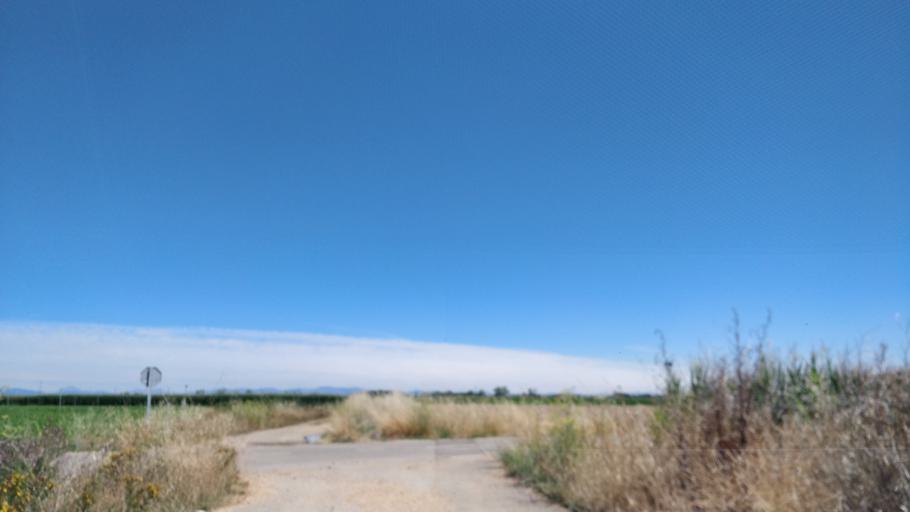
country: ES
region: Castille and Leon
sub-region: Provincia de Leon
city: Bustillo del Paramo
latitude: 42.4650
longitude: -5.8149
